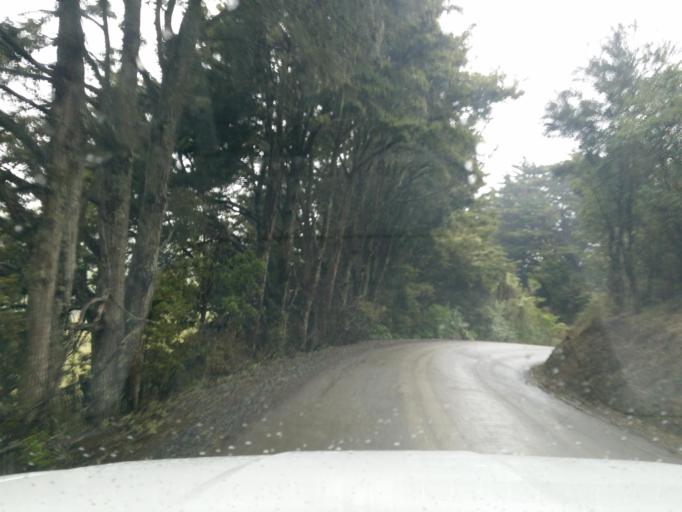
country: NZ
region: Northland
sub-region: Kaipara District
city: Dargaville
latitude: -35.9752
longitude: 174.0633
